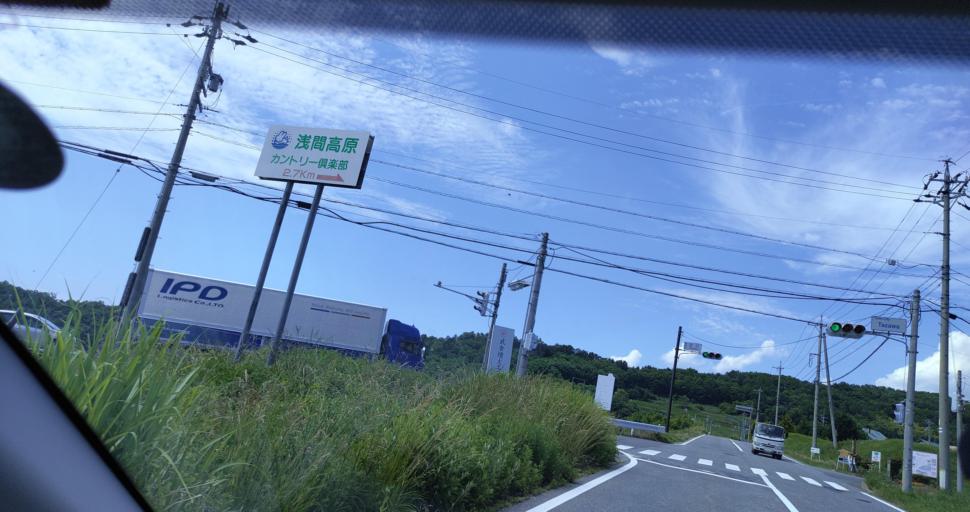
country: JP
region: Nagano
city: Ueda
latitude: 36.3864
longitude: 138.3280
